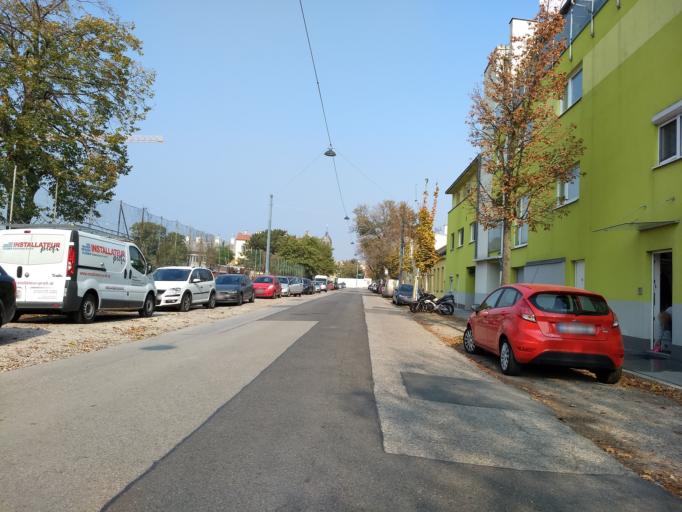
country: AT
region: Lower Austria
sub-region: Politischer Bezirk Modling
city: Brunn am Gebirge
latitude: 48.1326
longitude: 16.2887
